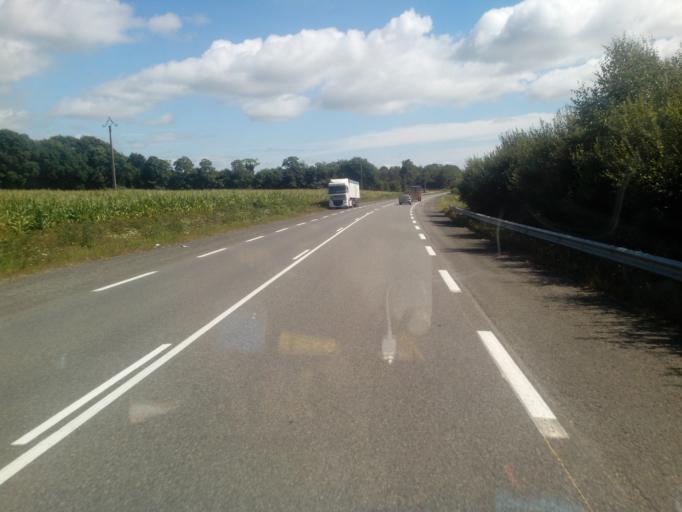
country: FR
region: Brittany
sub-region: Departement du Morbihan
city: Limerzel
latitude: 47.6108
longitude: -2.3896
